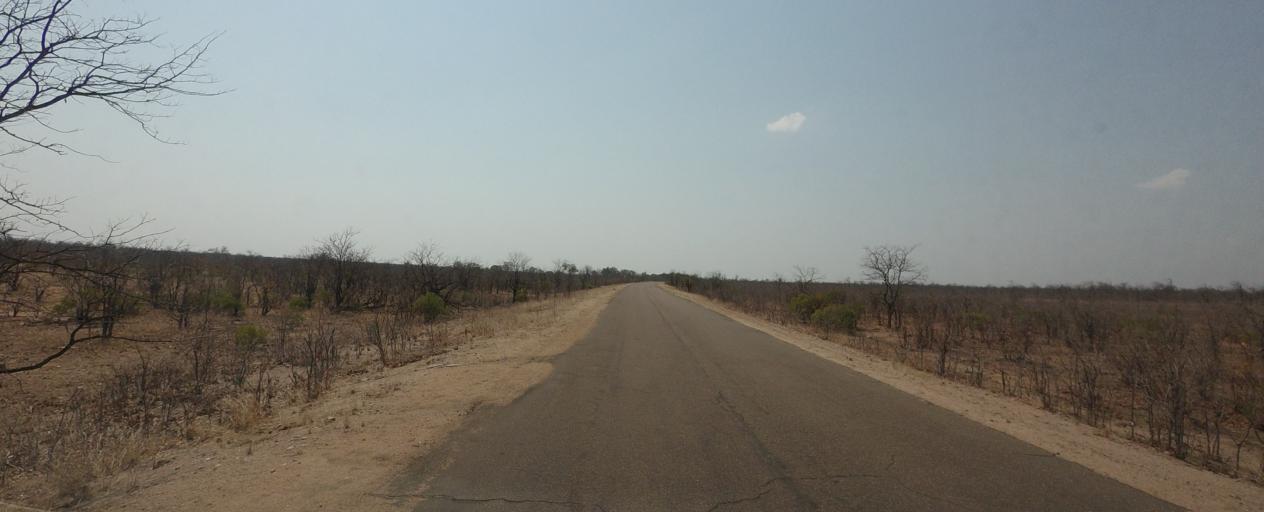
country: ZA
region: Limpopo
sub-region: Mopani District Municipality
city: Phalaborwa
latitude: -23.3758
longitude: 31.3223
